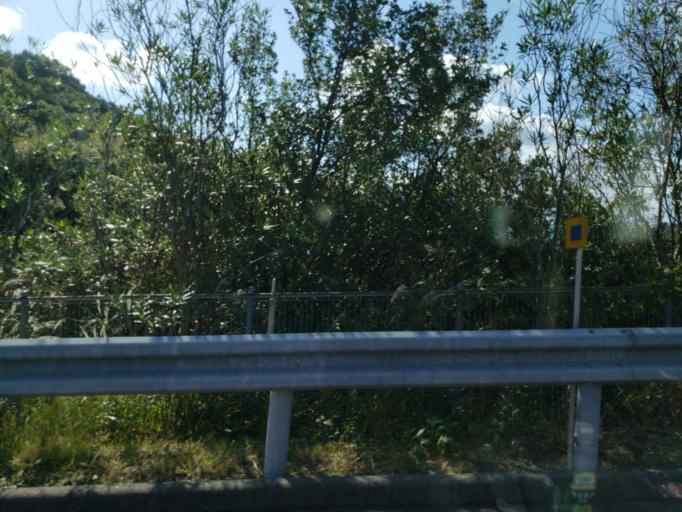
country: JP
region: Tokushima
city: Ishii
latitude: 34.1429
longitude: 134.4362
